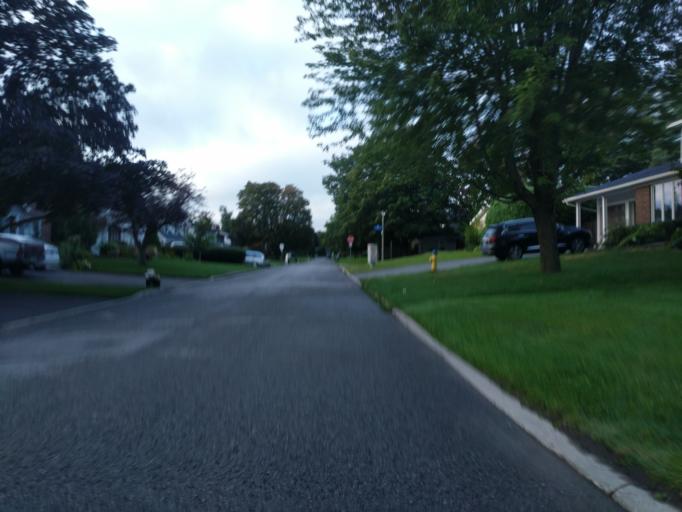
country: CA
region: Ontario
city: Bells Corners
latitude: 45.3441
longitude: -75.7986
